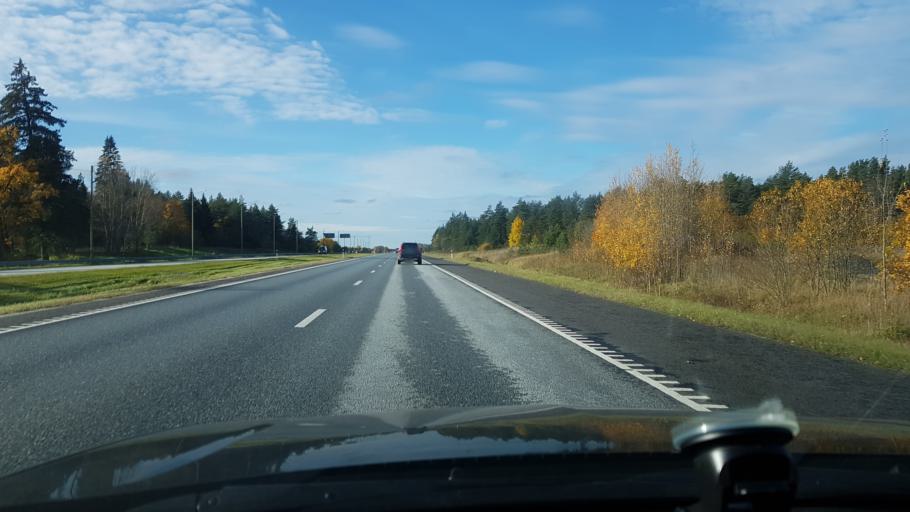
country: EE
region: Harju
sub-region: Kuusalu vald
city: Kuusalu
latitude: 59.4479
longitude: 25.4213
